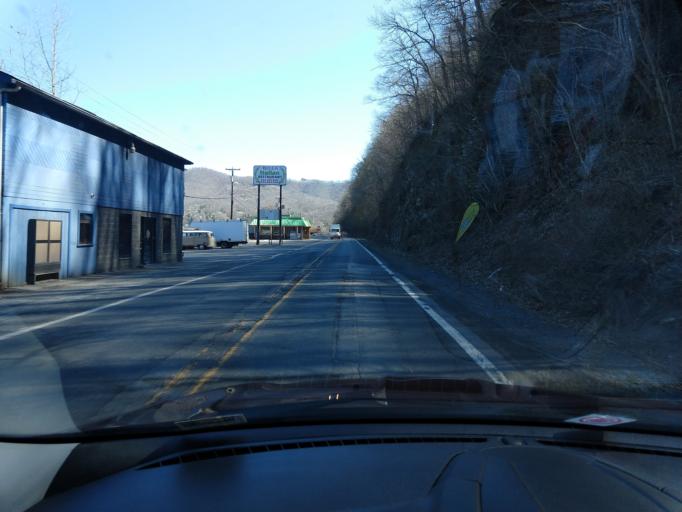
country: US
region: West Virginia
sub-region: Summers County
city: Hinton
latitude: 37.6559
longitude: -80.8943
